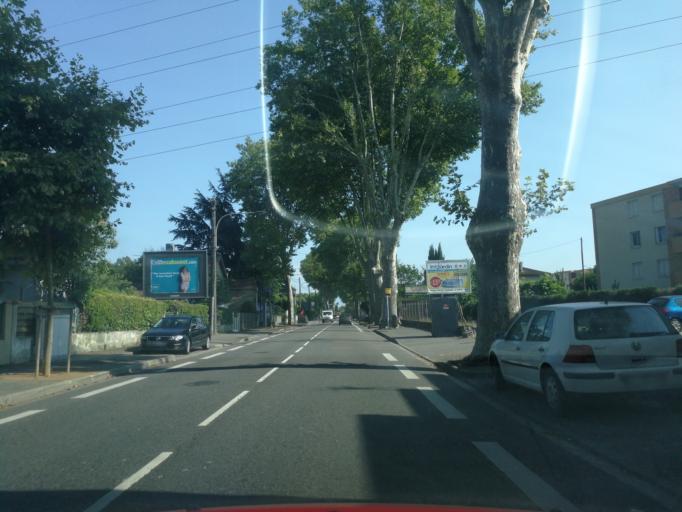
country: FR
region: Midi-Pyrenees
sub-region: Departement de la Haute-Garonne
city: Blagnac
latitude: 43.6215
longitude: 1.4057
